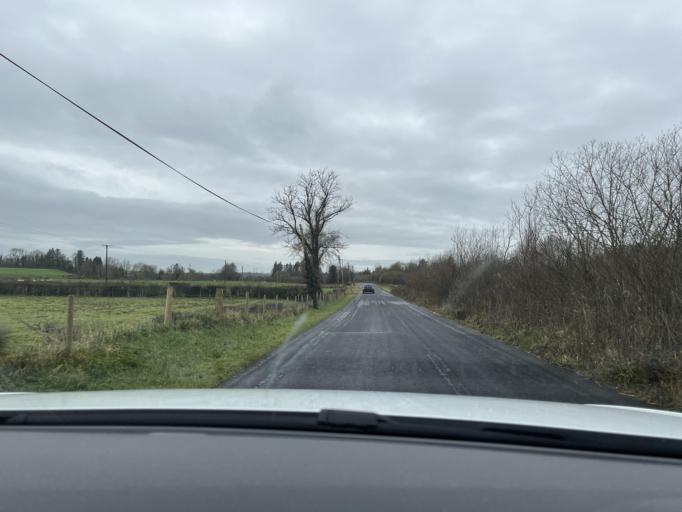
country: IE
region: Connaught
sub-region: County Leitrim
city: Manorhamilton
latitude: 54.2691
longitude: -8.2193
